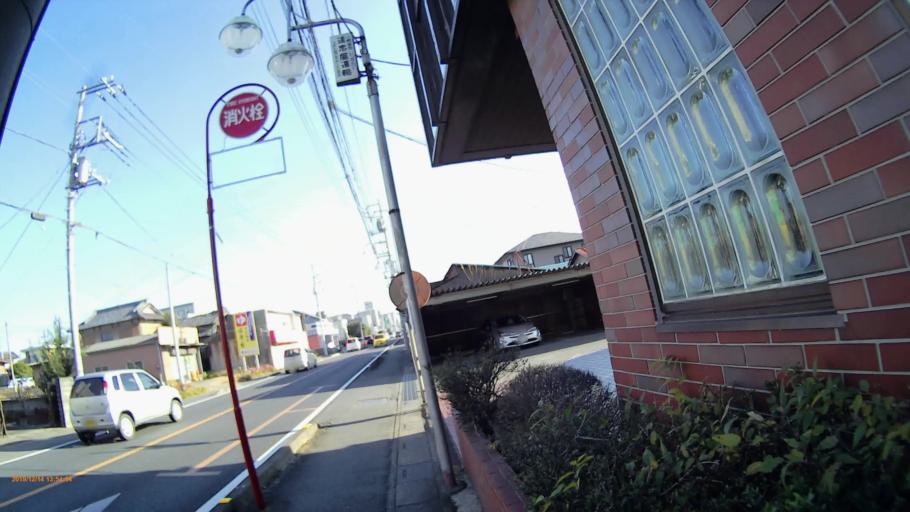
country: JP
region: Saitama
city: Konosu
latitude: 36.0656
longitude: 139.5068
